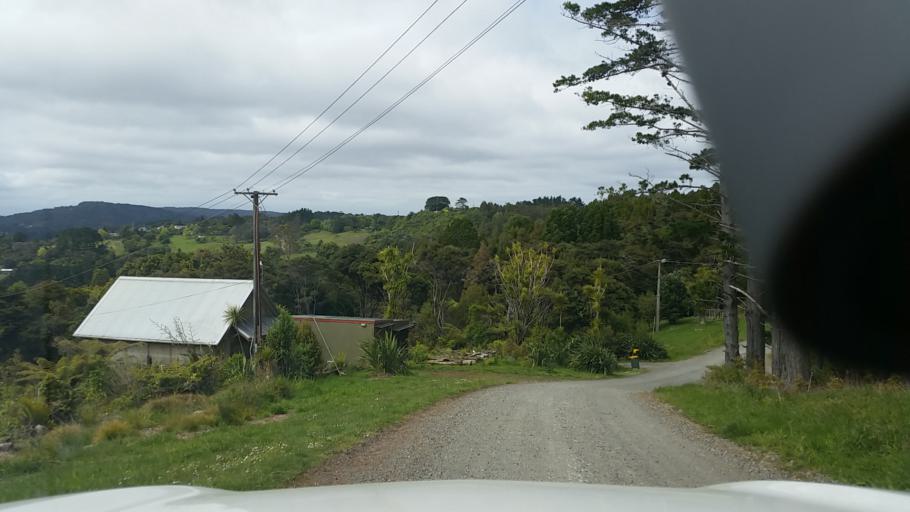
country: NZ
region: Auckland
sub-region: Auckland
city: Muriwai Beach
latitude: -36.8423
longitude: 174.5126
